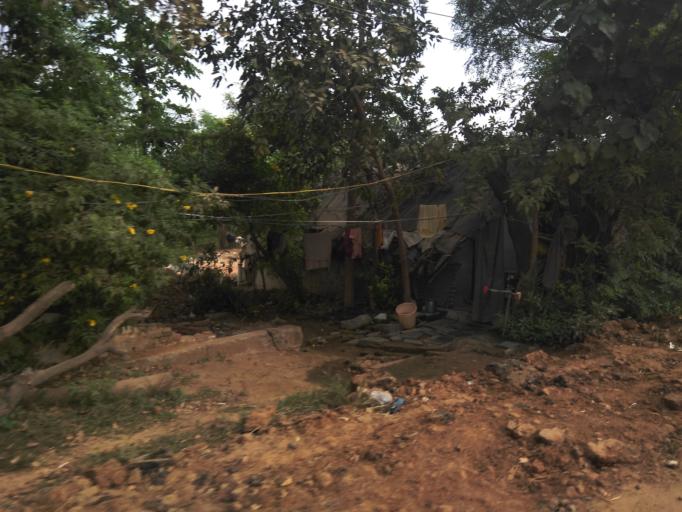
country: IN
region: Andhra Pradesh
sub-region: Nellore
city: Nellore
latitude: 14.4647
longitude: 79.9990
